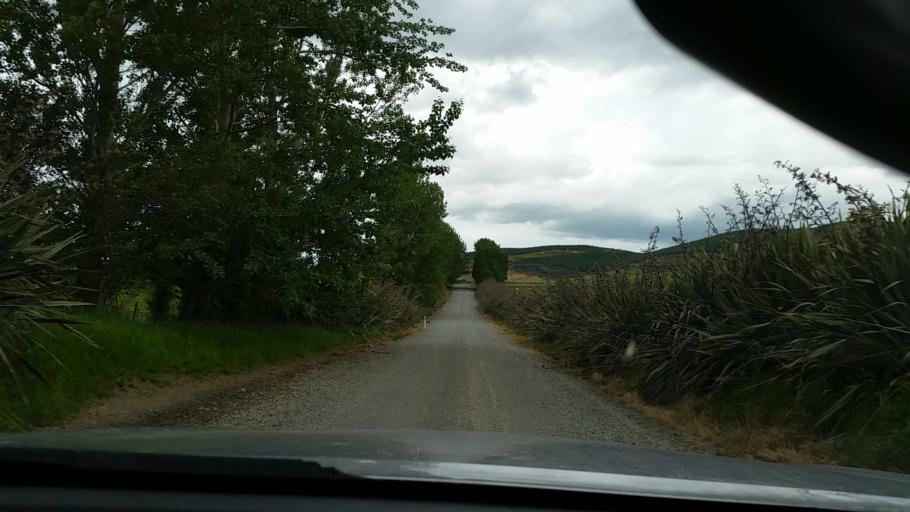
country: NZ
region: Southland
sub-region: Southland District
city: Winton
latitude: -45.8132
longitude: 168.1995
